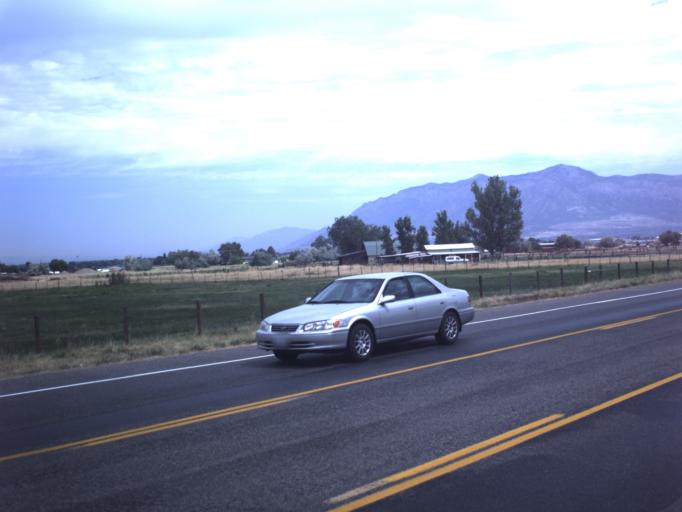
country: US
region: Utah
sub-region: Weber County
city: West Haven
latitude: 41.1991
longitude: -112.0381
